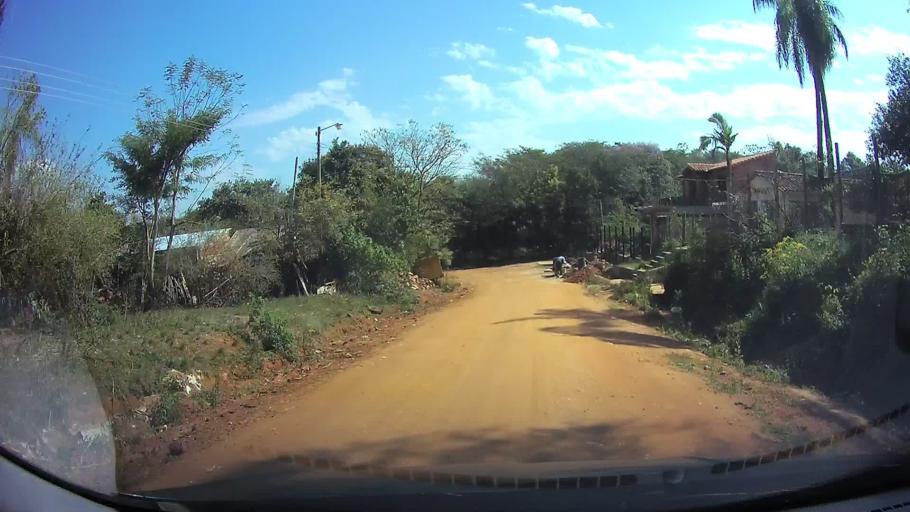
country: PY
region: Central
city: Limpio
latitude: -25.2251
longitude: -57.4395
